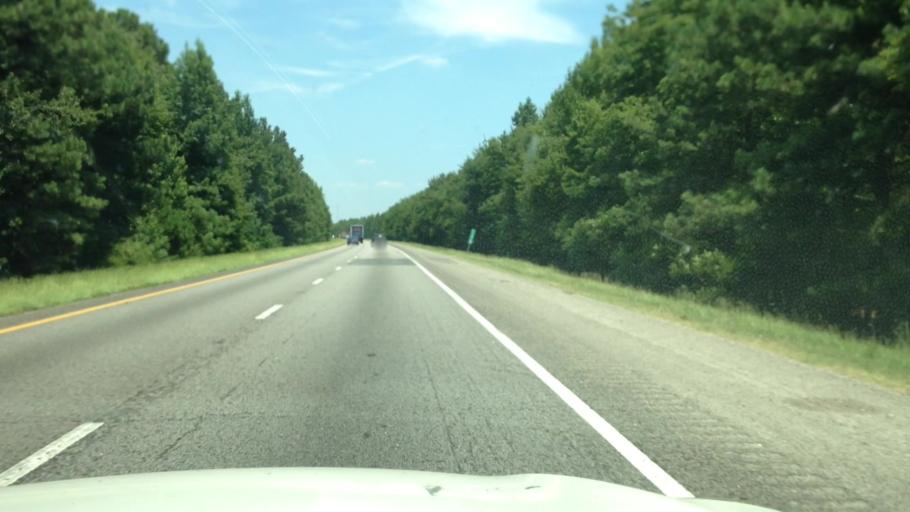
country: US
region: South Carolina
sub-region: Dillon County
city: Latta
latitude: 34.3194
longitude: -79.5885
